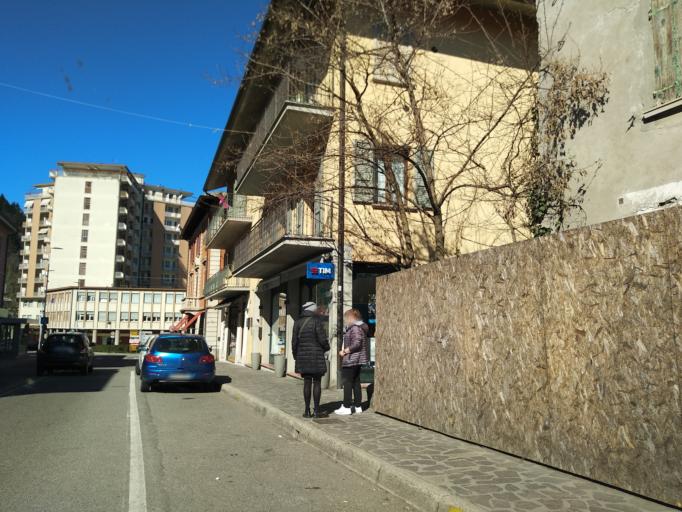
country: IT
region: Emilia-Romagna
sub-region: Provincia di Reggio Emilia
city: Castelnovo ne'Monti
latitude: 44.4363
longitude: 10.4038
